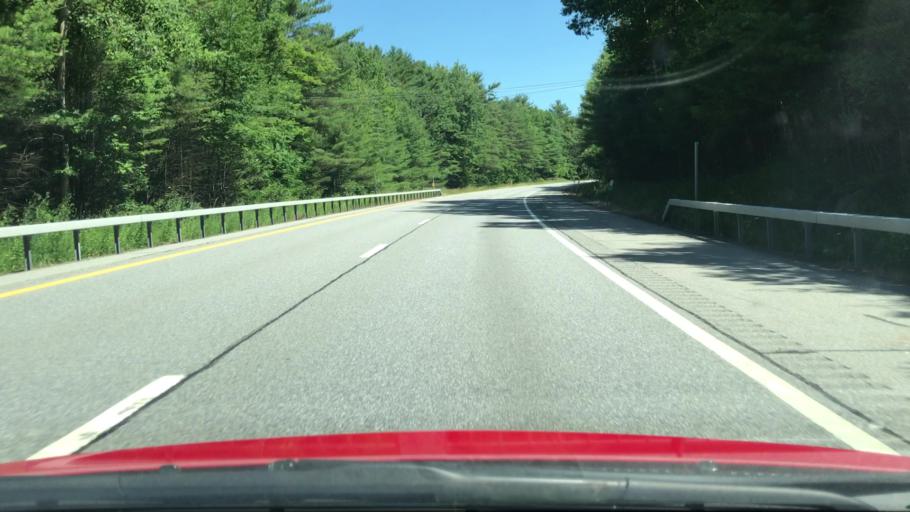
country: US
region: New York
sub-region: Warren County
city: Warrensburg
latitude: 43.5119
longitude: -73.7434
